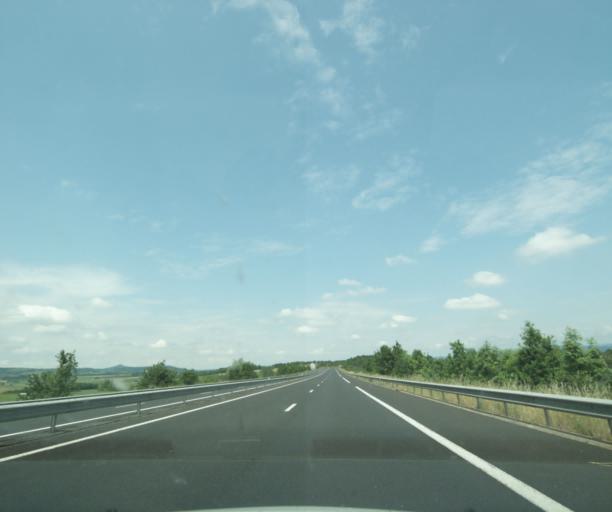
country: FR
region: Auvergne
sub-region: Departement de la Haute-Loire
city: Lempdes-sur-Allagnon
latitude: 45.3495
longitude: 3.2775
